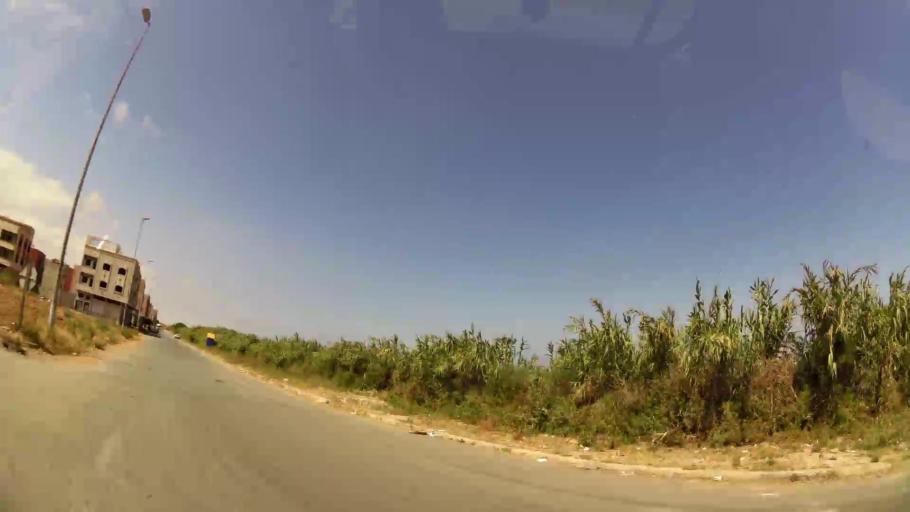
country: MA
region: Rabat-Sale-Zemmour-Zaer
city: Sale
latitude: 34.0753
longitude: -6.7734
